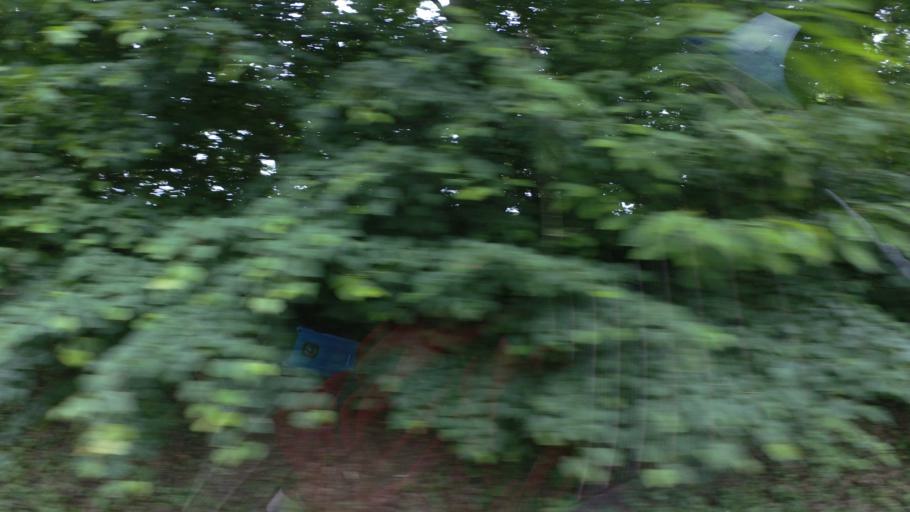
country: HR
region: Karlovacka
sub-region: Grad Karlovac
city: Karlovac
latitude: 45.4165
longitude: 15.5920
